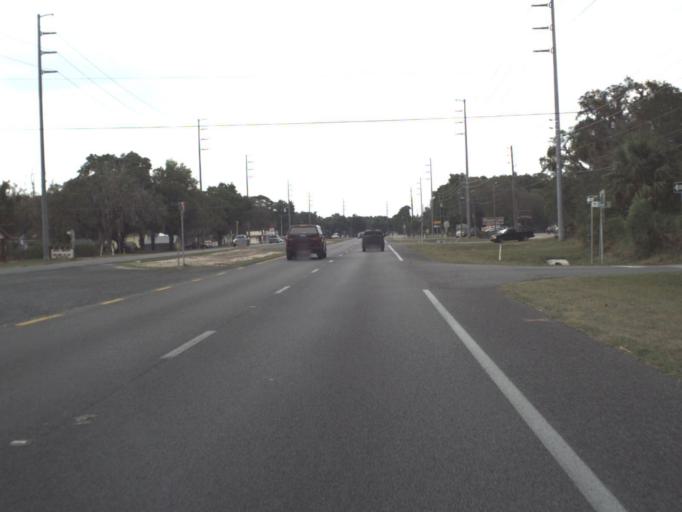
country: US
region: Florida
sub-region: Lake County
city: Eustis
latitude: 28.8935
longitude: -81.6868
